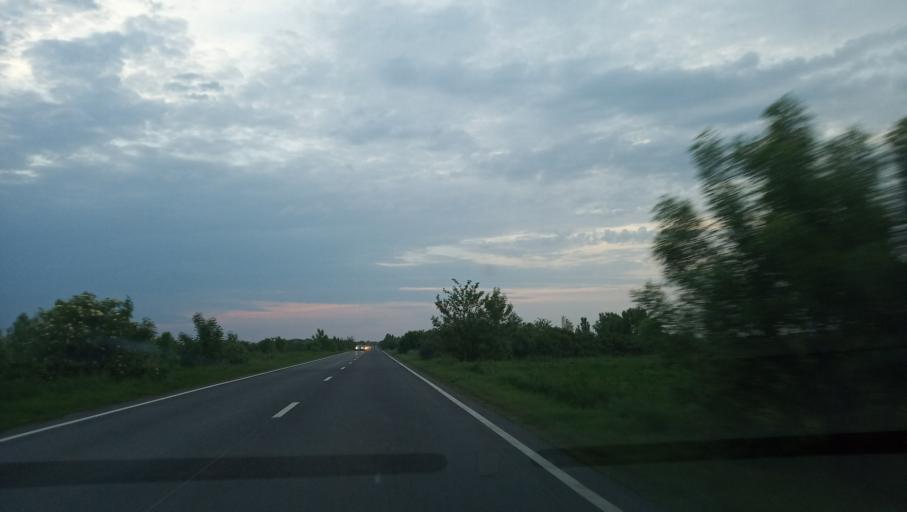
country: RO
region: Timis
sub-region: Comuna Jebel
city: Jebel
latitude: 45.5440
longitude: 21.2251
